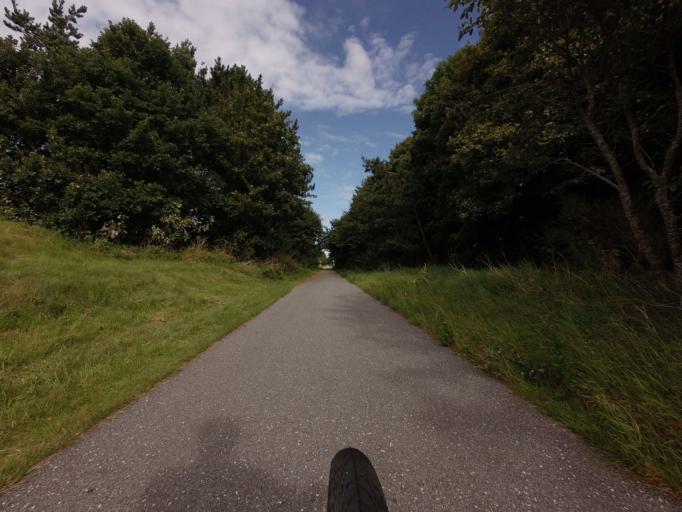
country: DK
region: Central Jutland
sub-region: Norddjurs Kommune
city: Auning
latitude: 56.4333
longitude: 10.3742
